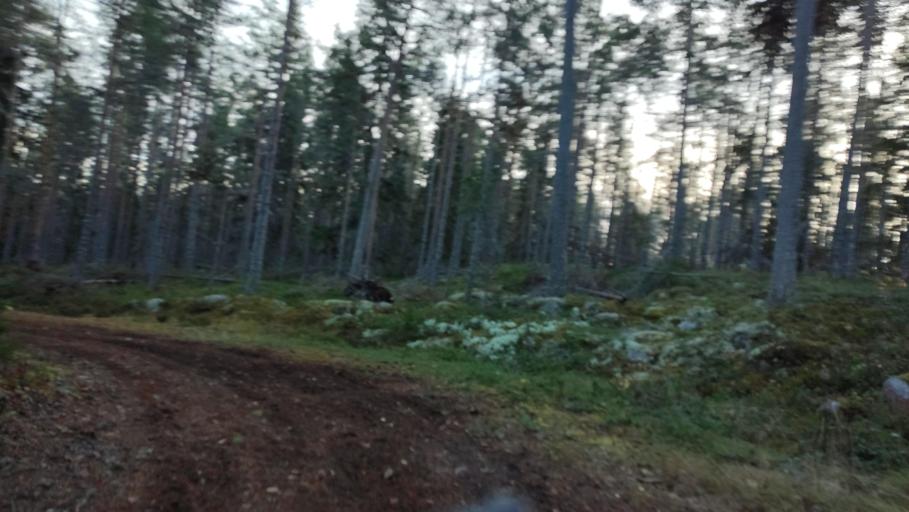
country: FI
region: Southern Ostrobothnia
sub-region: Suupohja
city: Karijoki
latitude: 62.2742
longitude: 21.6305
